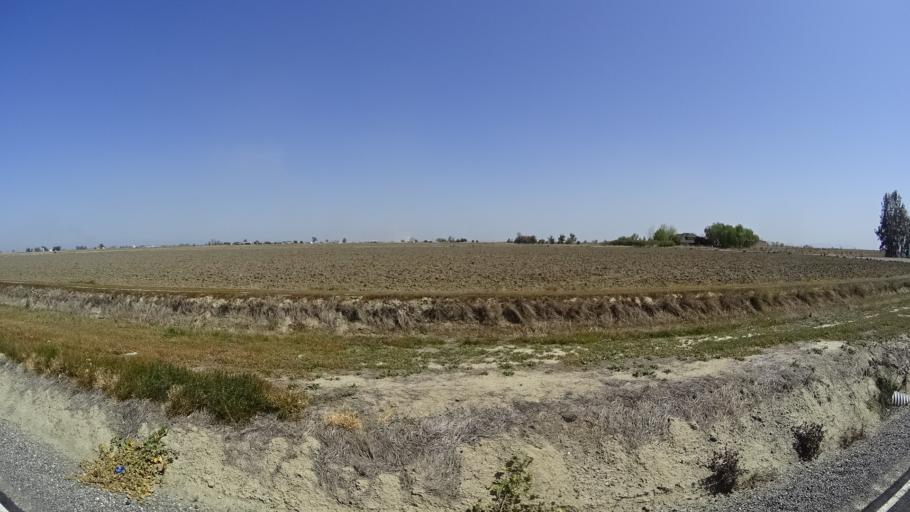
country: US
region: California
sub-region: Glenn County
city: Willows
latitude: 39.5317
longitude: -122.1369
